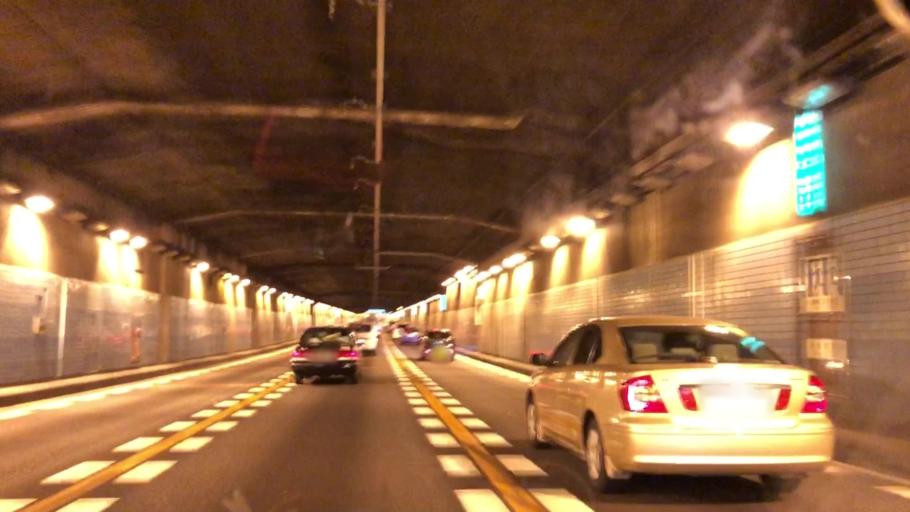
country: JP
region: Tokyo
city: Tokyo
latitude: 35.6157
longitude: 139.7608
